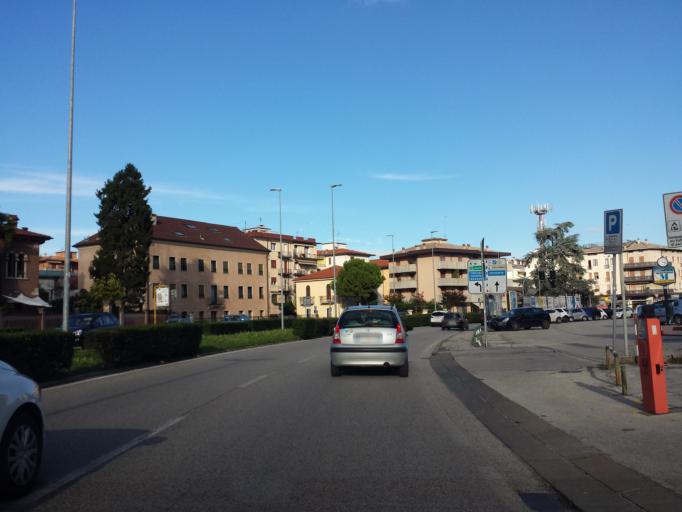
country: IT
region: Veneto
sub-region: Provincia di Vicenza
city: Vicenza
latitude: 45.5579
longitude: 11.5428
